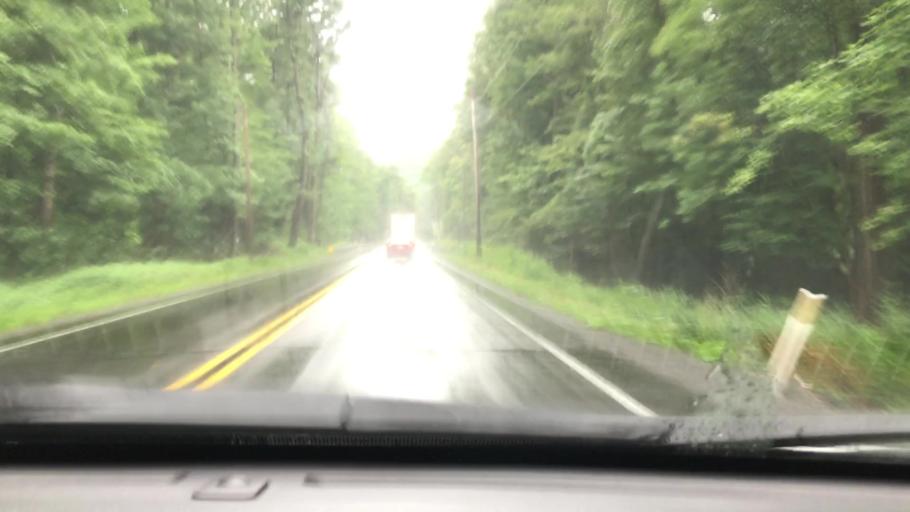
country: US
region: Pennsylvania
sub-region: Blair County
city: Tyrone
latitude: 40.7594
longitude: -78.2282
